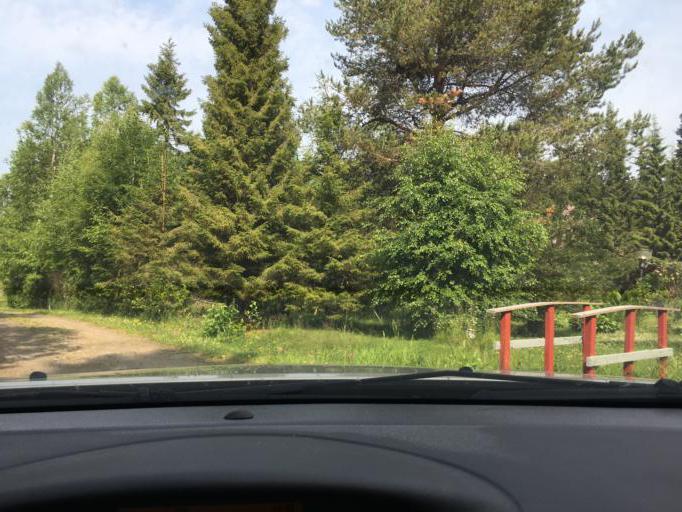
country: SE
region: Norrbotten
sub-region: Kalix Kommun
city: Rolfs
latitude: 65.7572
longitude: 23.0024
